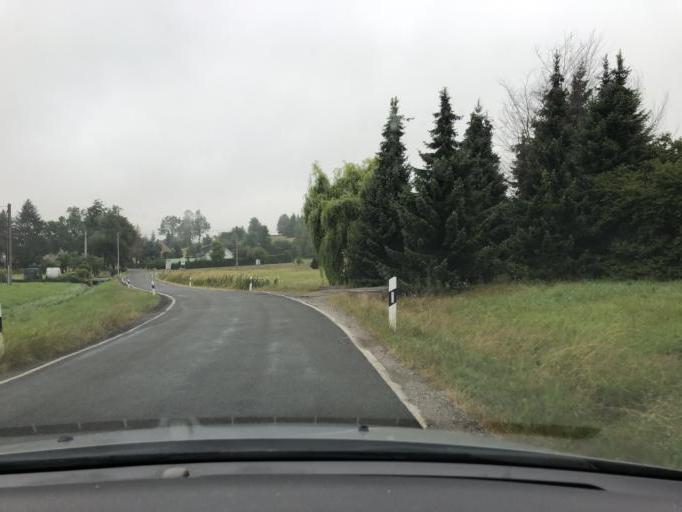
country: DE
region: Saxony
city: Narsdorf
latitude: 50.9957
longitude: 12.6823
